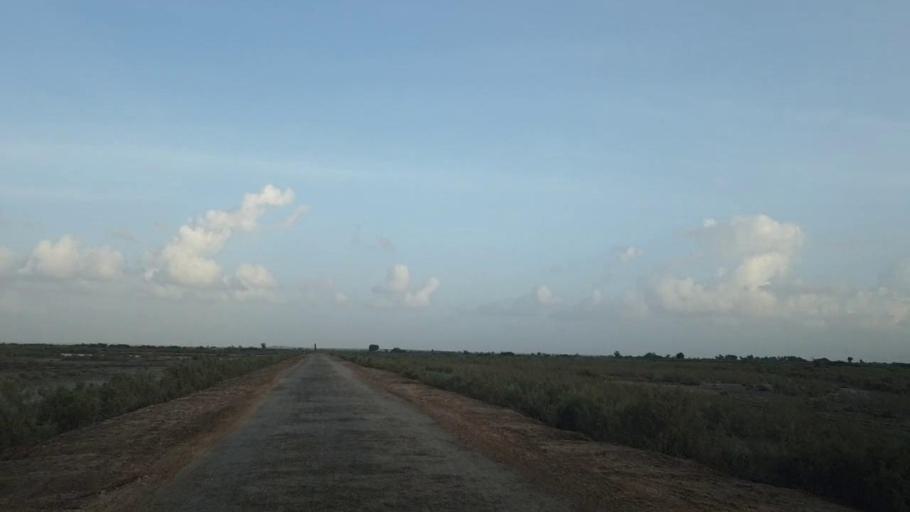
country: PK
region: Sindh
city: Kadhan
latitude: 24.5665
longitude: 69.1197
